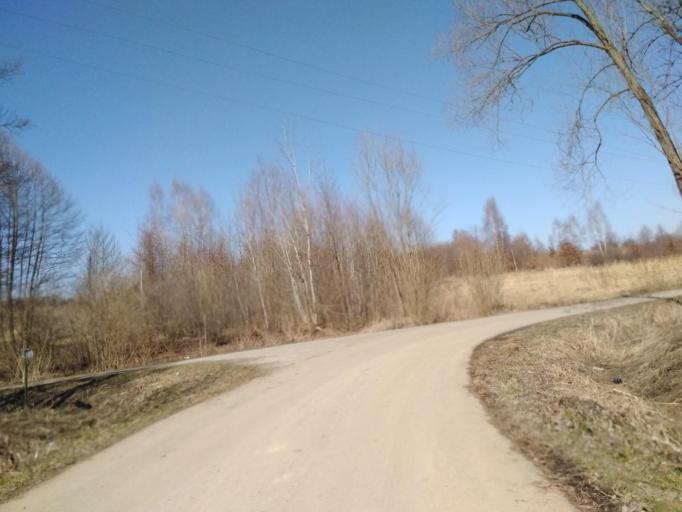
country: PL
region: Subcarpathian Voivodeship
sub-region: Powiat brzozowski
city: Orzechowka
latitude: 49.7096
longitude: 21.9667
